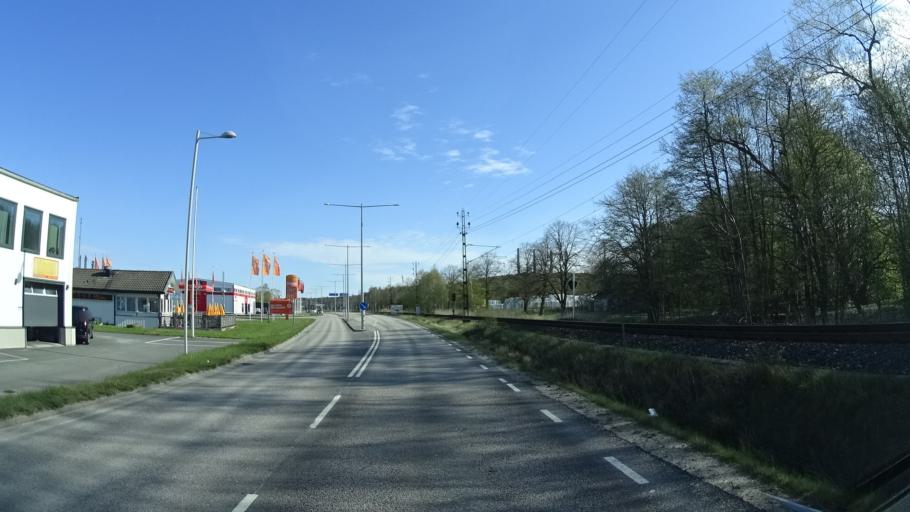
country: SE
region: Vaestra Goetaland
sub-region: Stenungsunds Kommun
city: Stenungsund
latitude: 58.0765
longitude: 11.8283
